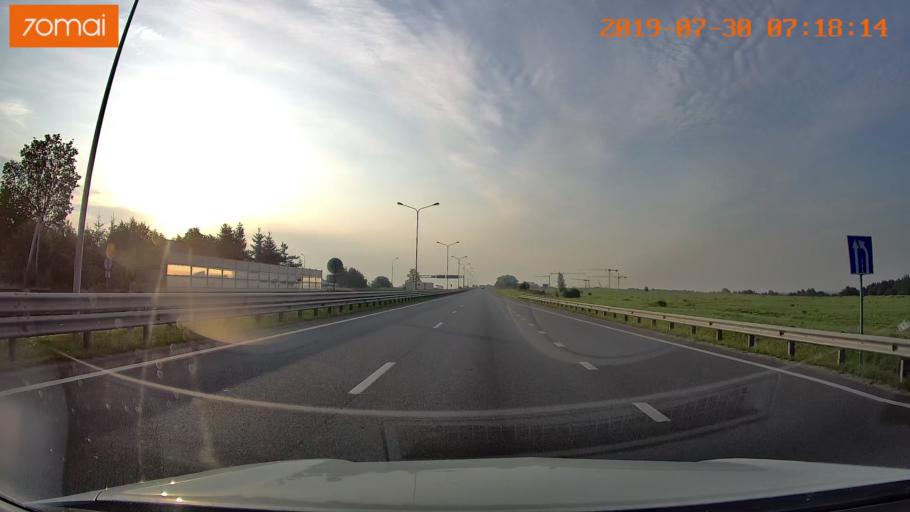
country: RU
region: Kaliningrad
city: Bol'shoe Isakovo
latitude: 54.7049
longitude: 20.6438
